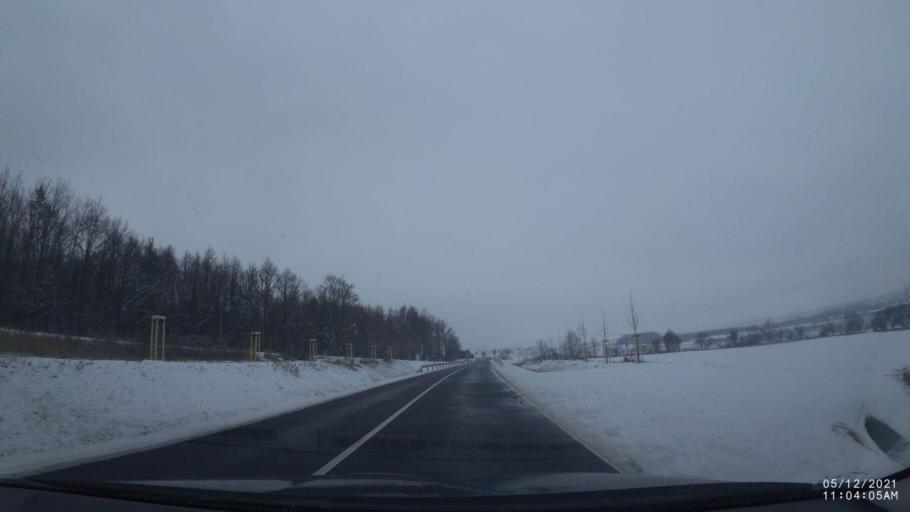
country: CZ
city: Solnice
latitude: 50.1731
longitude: 16.2219
